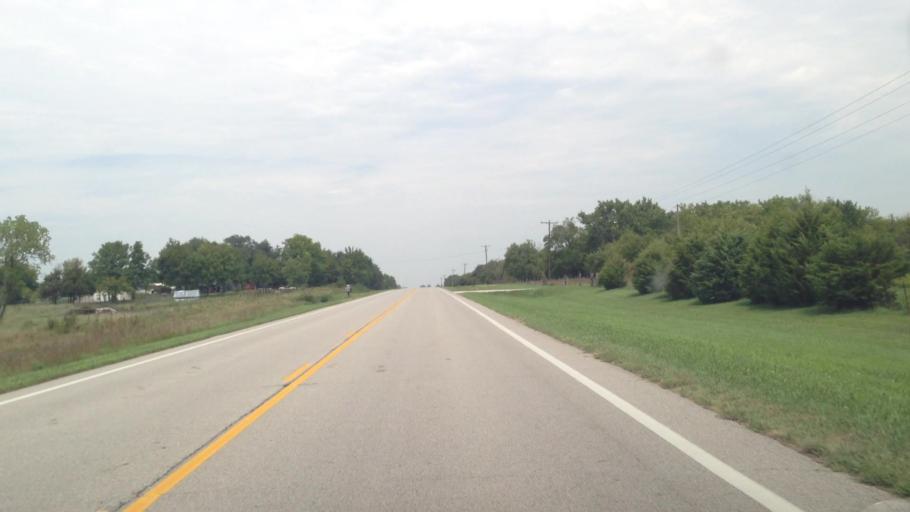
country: US
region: Kansas
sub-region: Neosho County
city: Erie
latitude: 37.6505
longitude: -95.2516
